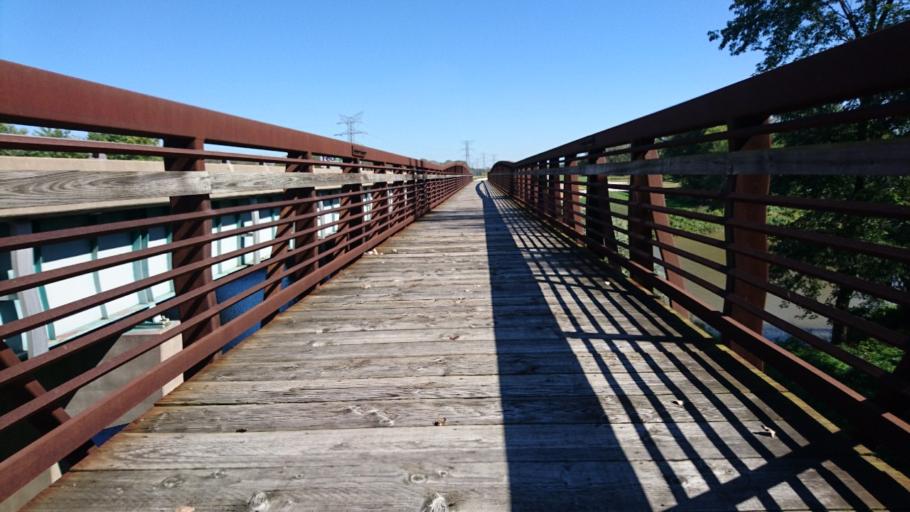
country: US
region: Illinois
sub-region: Madison County
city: East Alton
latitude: 38.8613
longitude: -90.1295
